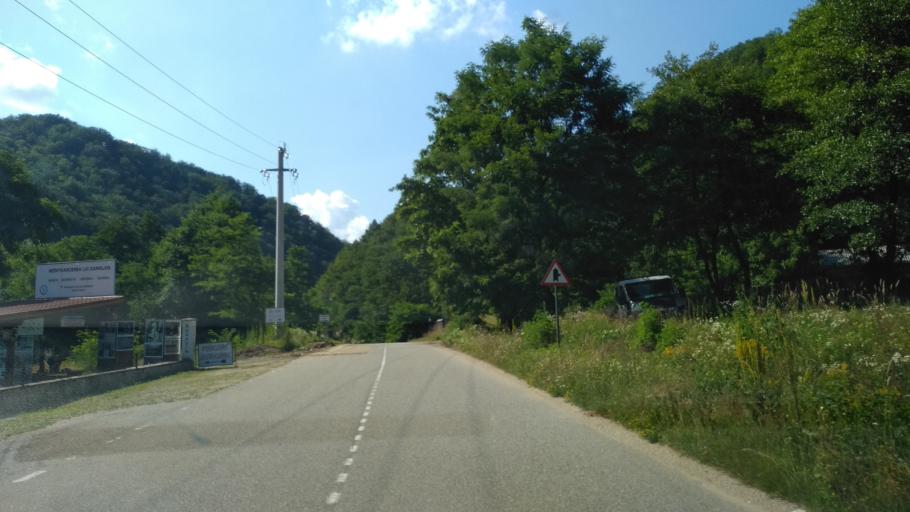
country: RO
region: Hunedoara
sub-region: Comuna Orastioara de Sus
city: Orastioara de Sus
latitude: 45.6701
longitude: 23.1717
